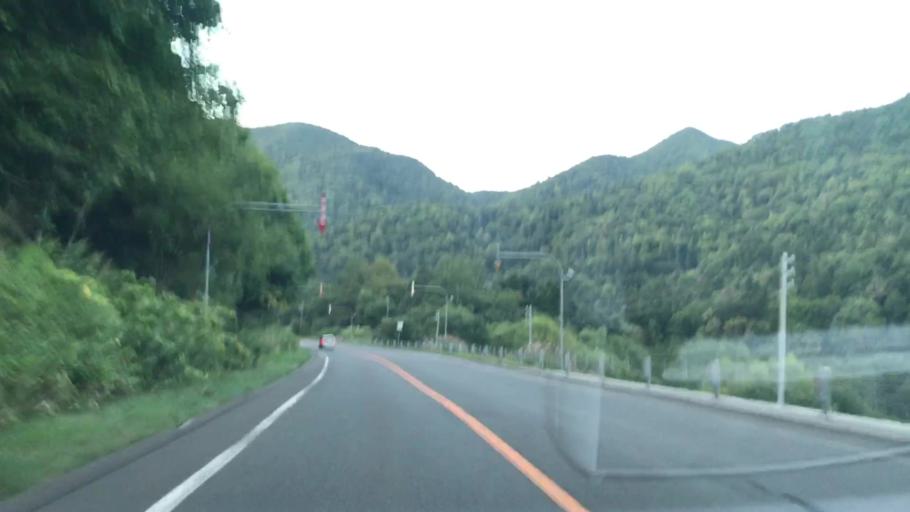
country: JP
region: Hokkaido
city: Sapporo
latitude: 42.9144
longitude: 141.1229
